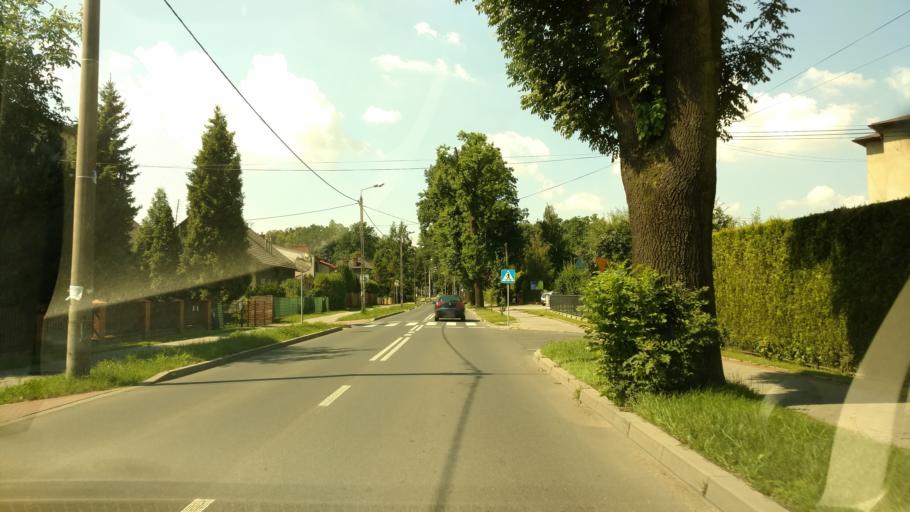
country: PL
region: Silesian Voivodeship
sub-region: Powiat pszczynski
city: Pszczyna
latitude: 49.9874
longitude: 18.9501
